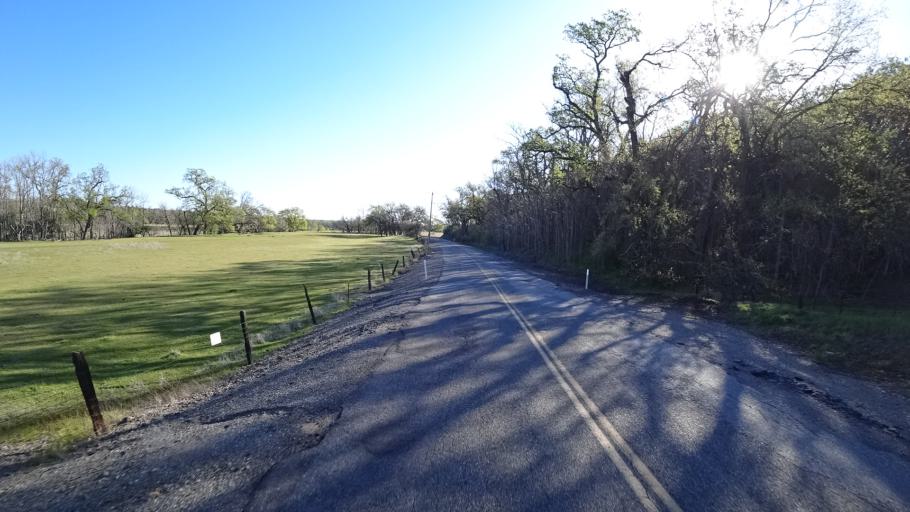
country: US
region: California
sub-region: Tehama County
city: Rancho Tehama Reserve
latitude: 39.7945
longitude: -122.4446
